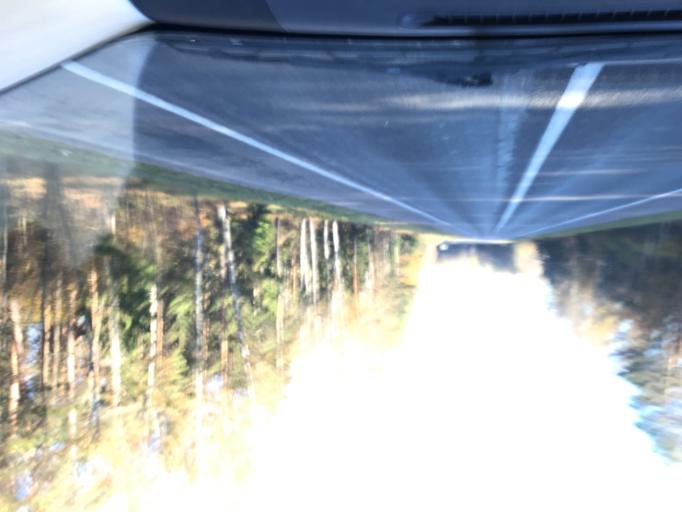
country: BY
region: Vitebsk
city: Syanno
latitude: 55.1135
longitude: 29.7631
